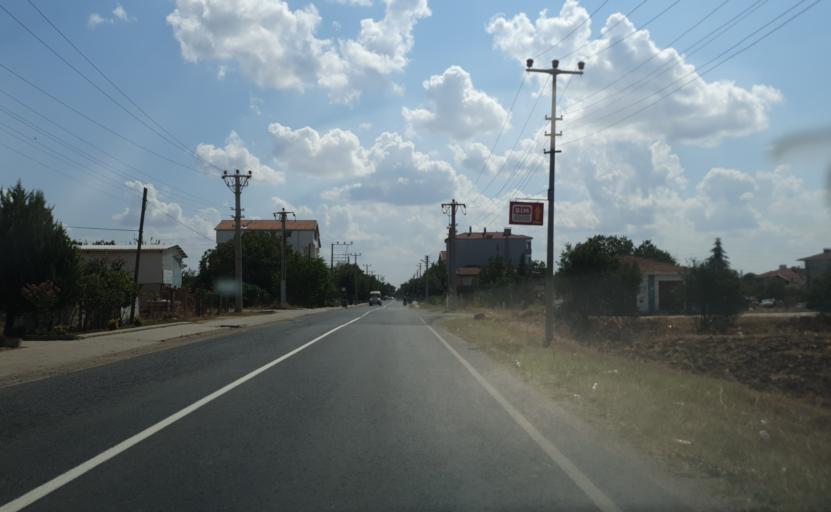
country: TR
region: Kirklareli
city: Luleburgaz
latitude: 41.3628
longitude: 27.3374
